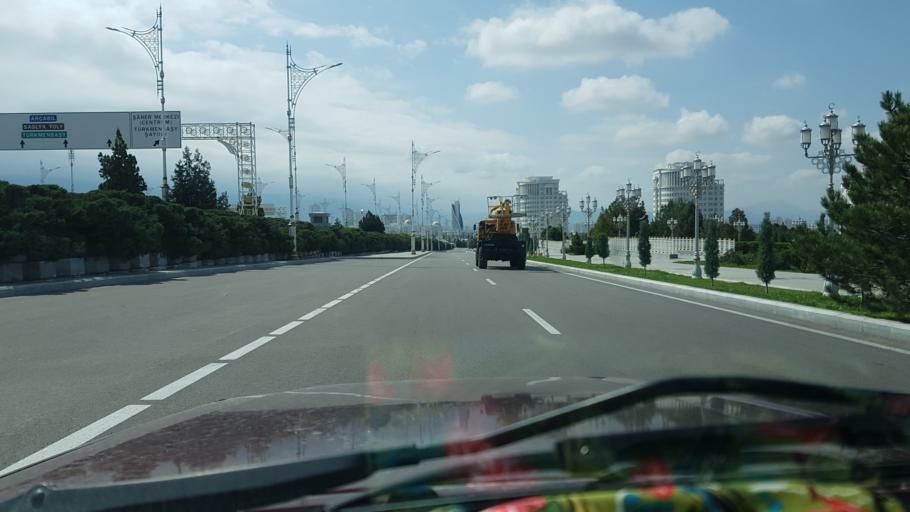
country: TM
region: Ahal
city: Ashgabat
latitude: 37.8794
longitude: 58.3837
